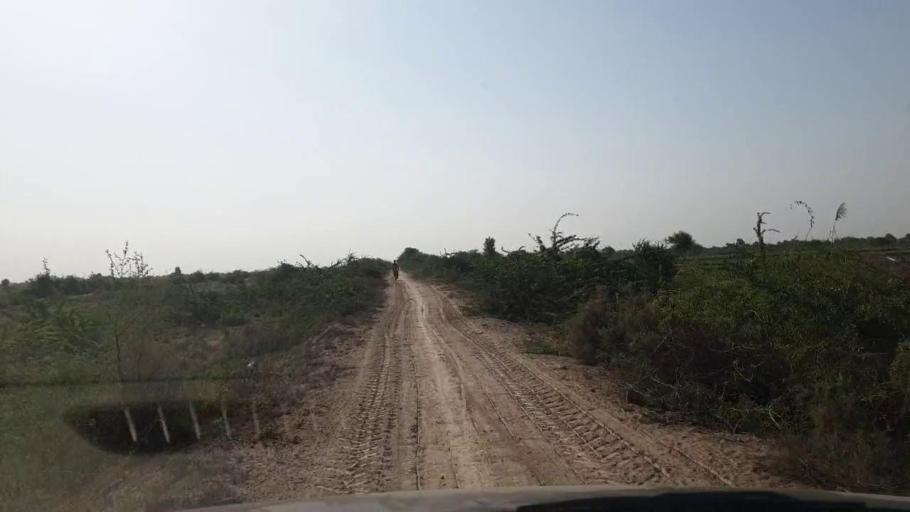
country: PK
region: Sindh
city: Kadhan
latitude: 24.5900
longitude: 69.0769
